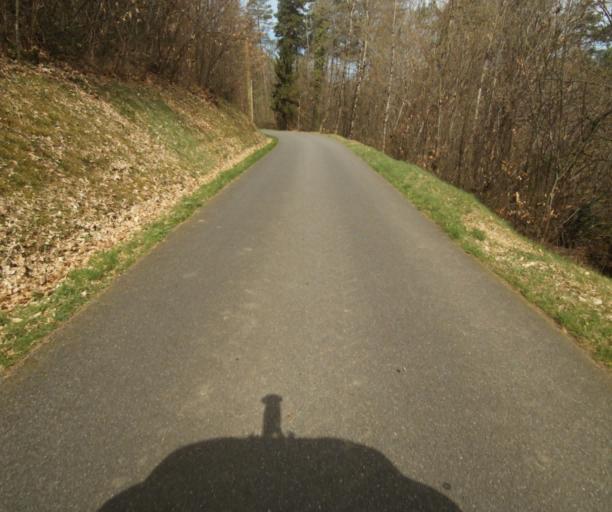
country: FR
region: Limousin
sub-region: Departement de la Correze
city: Naves
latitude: 45.3325
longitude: 1.8033
